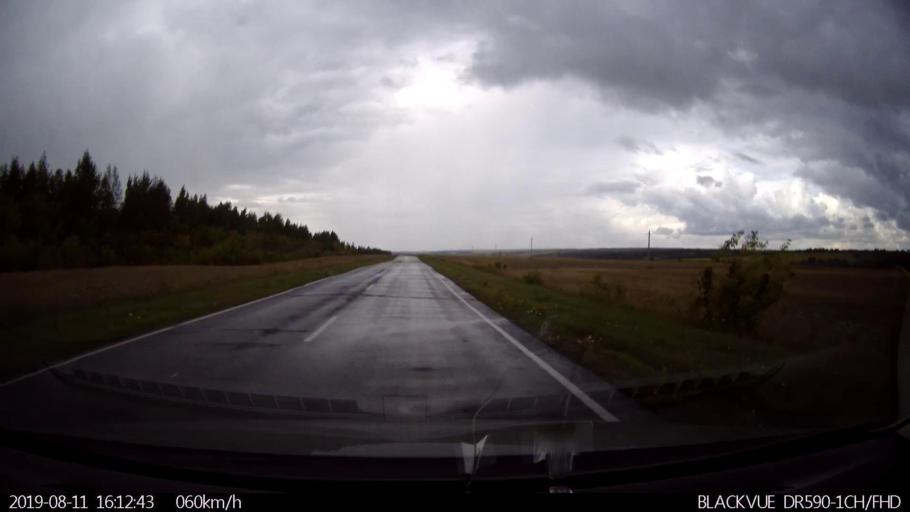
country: RU
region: Ulyanovsk
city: Ignatovka
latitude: 54.0139
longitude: 47.6395
